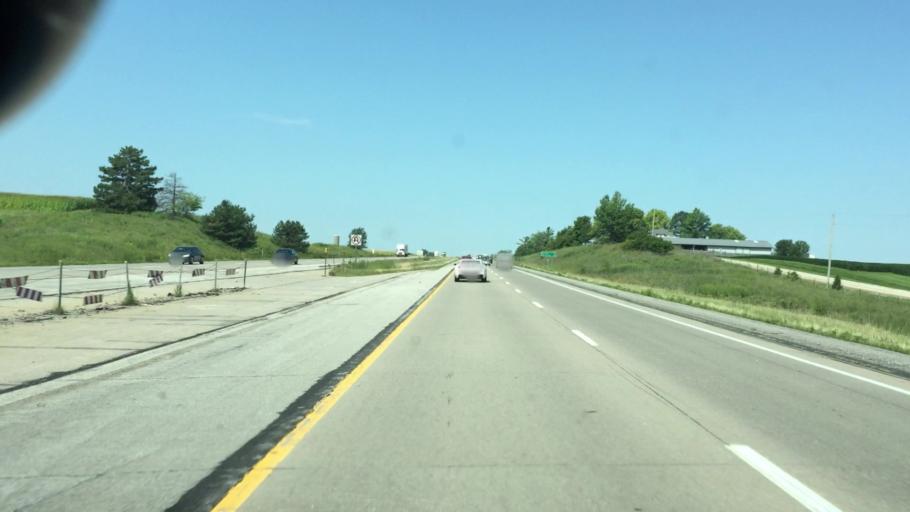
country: US
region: Iowa
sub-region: Iowa County
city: Williamsburg
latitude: 41.6873
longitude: -92.0225
